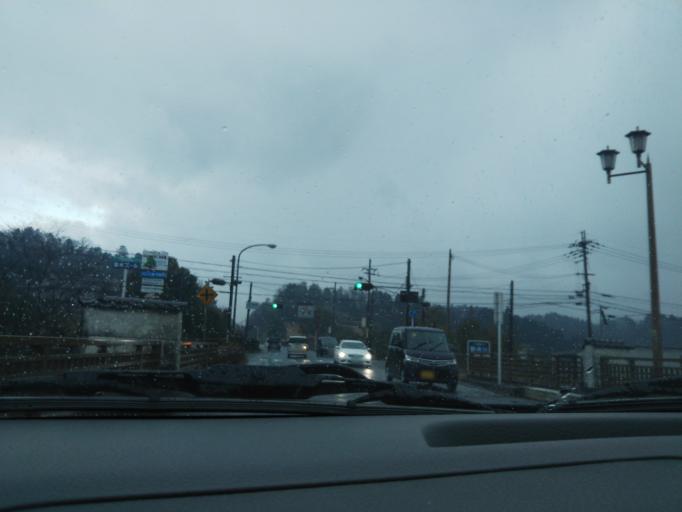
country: JP
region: Shiga Prefecture
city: Minakuchicho-matoba
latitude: 34.9610
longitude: 136.1661
